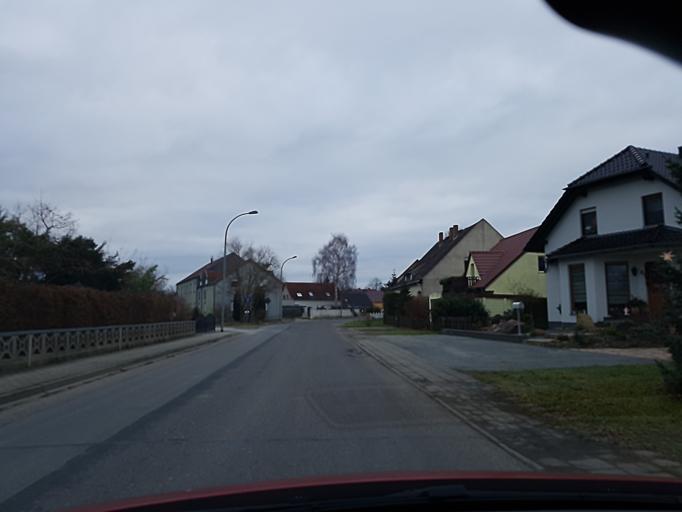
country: DE
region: Brandenburg
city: Elsterwerda
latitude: 51.4502
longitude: 13.5066
